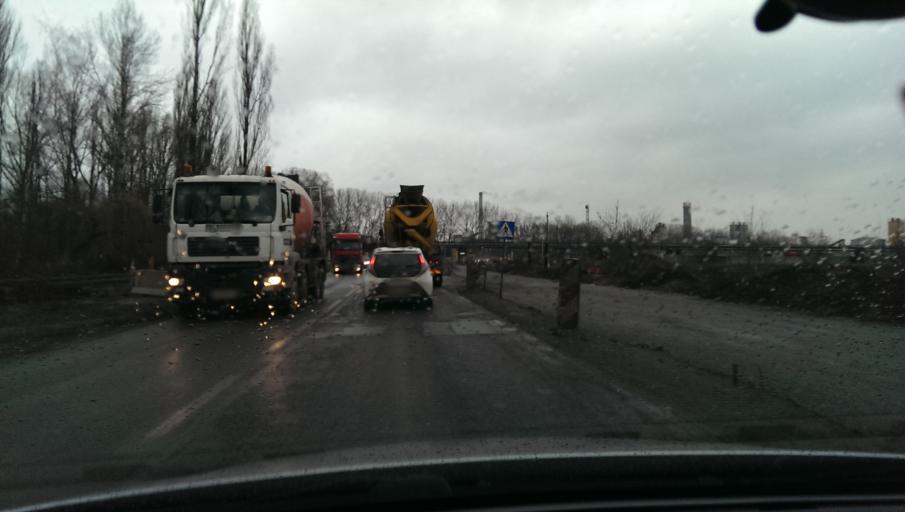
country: PL
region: Lesser Poland Voivodeship
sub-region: Powiat wielicki
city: Kokotow
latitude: 50.0675
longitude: 20.0905
